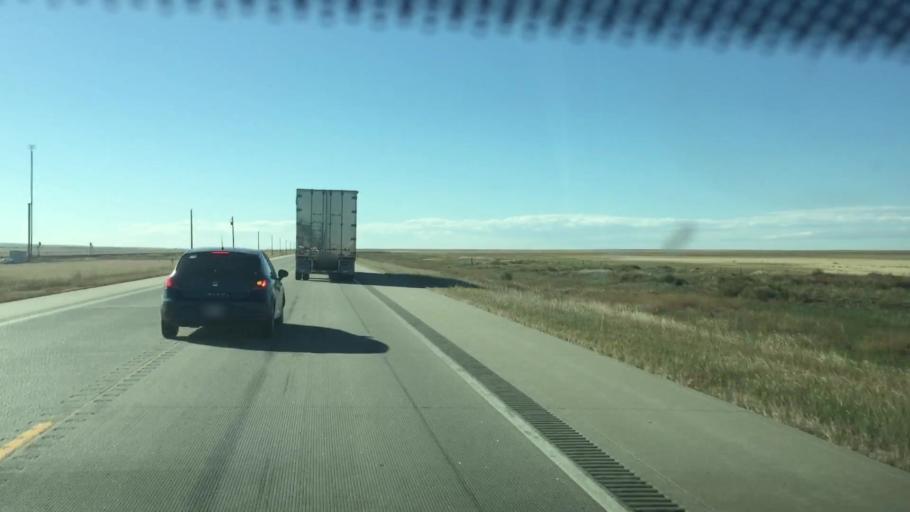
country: US
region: Colorado
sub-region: Kiowa County
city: Eads
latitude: 38.8304
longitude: -103.0401
